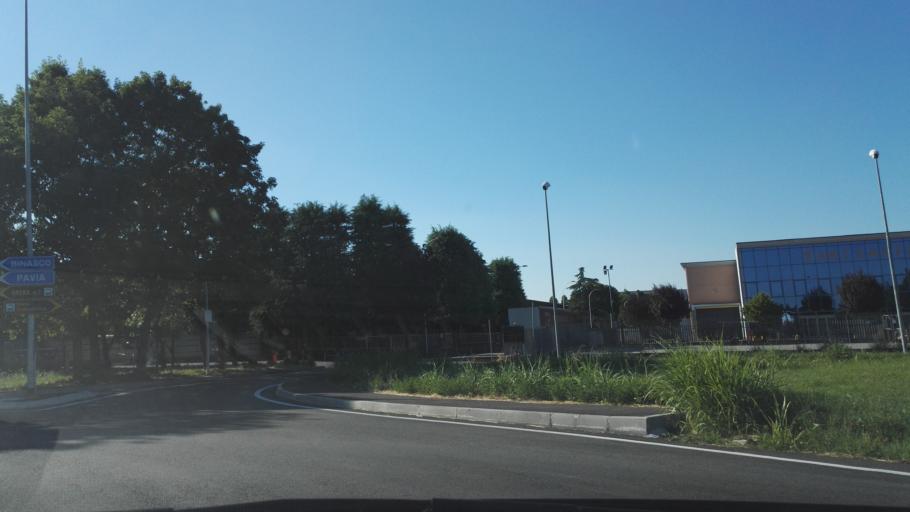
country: IT
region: Lombardy
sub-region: Citta metropolitana di Milano
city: Opera
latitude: 45.3701
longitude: 9.2193
